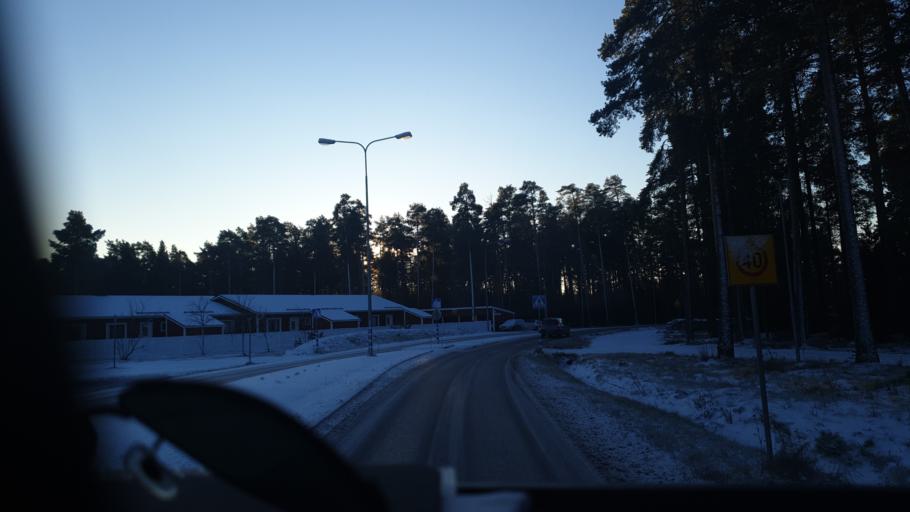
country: FI
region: Central Ostrobothnia
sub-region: Kokkola
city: Kokkola
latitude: 63.8295
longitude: 23.1032
